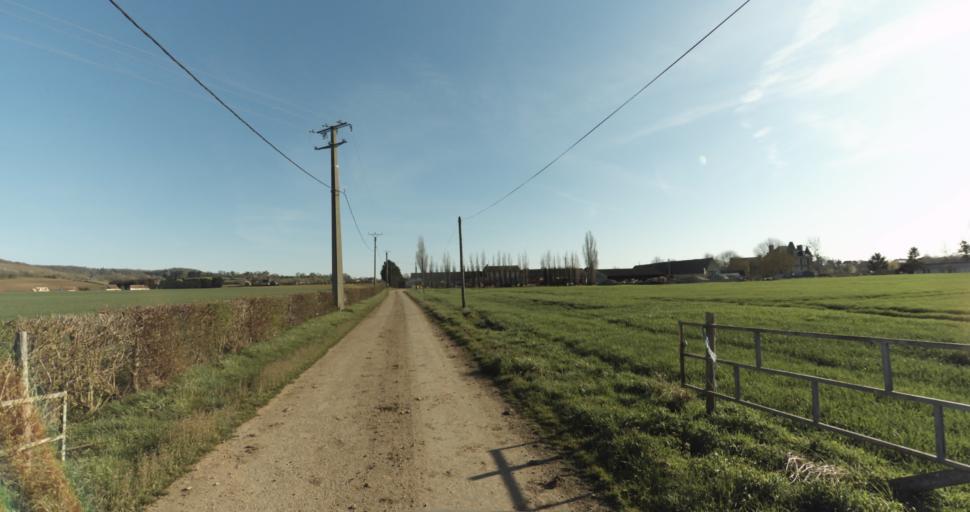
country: FR
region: Lower Normandy
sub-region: Departement du Calvados
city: Saint-Pierre-sur-Dives
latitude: 49.0170
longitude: 0.0234
